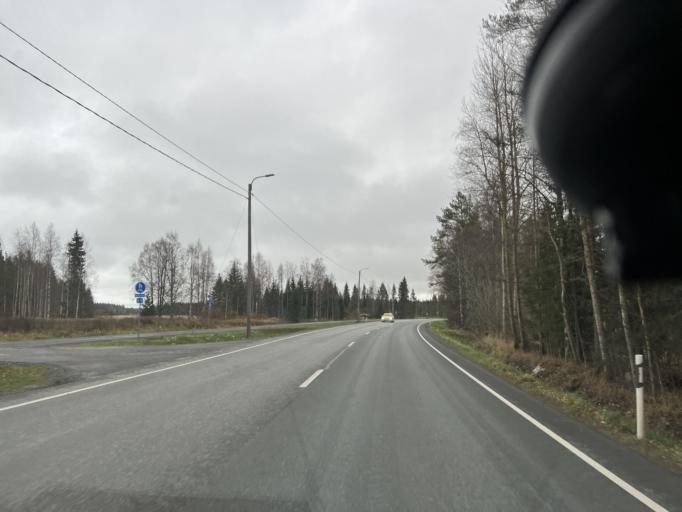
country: FI
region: Northern Ostrobothnia
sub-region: Ylivieska
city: Sievi
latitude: 63.9439
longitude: 24.5292
